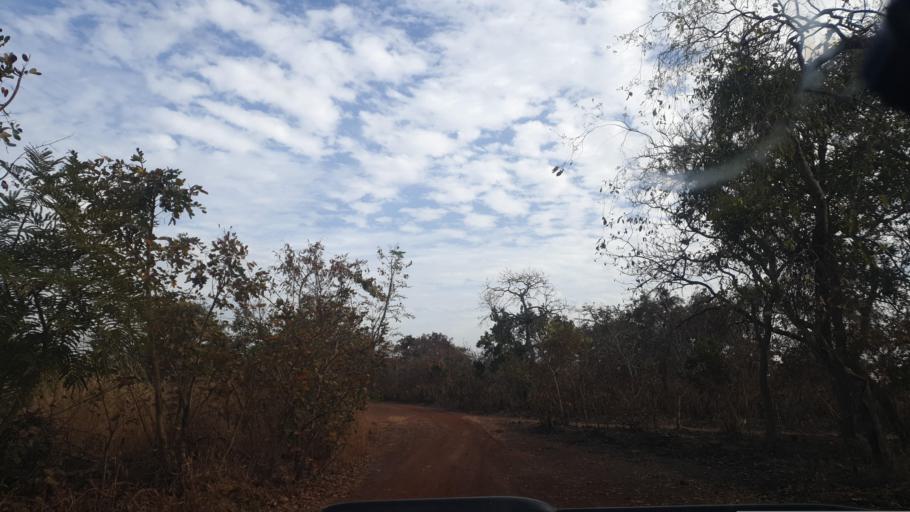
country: ML
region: Sikasso
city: Yanfolila
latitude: 11.3931
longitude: -8.0210
